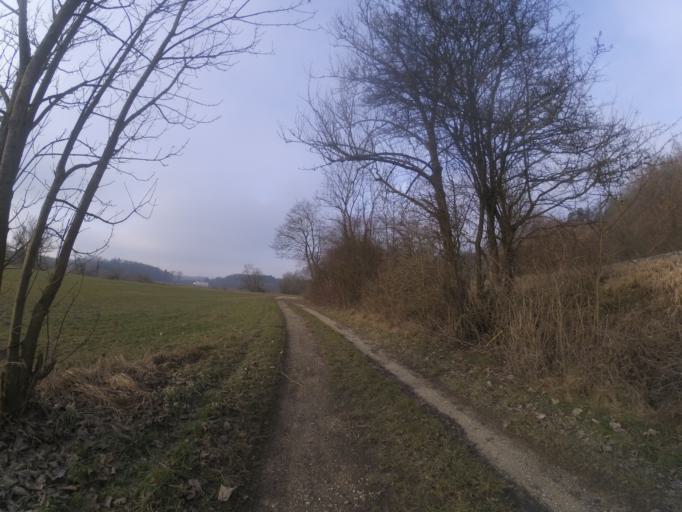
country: DE
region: Baden-Wuerttemberg
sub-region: Tuebingen Region
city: Lauterach
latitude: 48.2440
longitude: 9.5866
